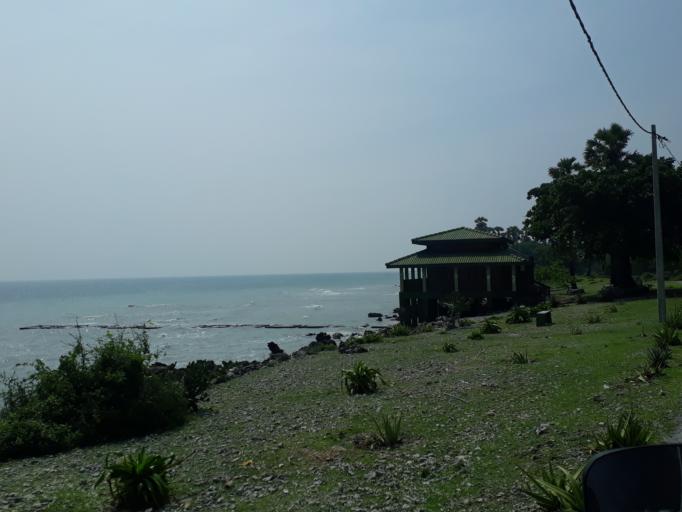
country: LK
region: Northern Province
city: Jaffna
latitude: 9.5204
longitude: 79.7256
